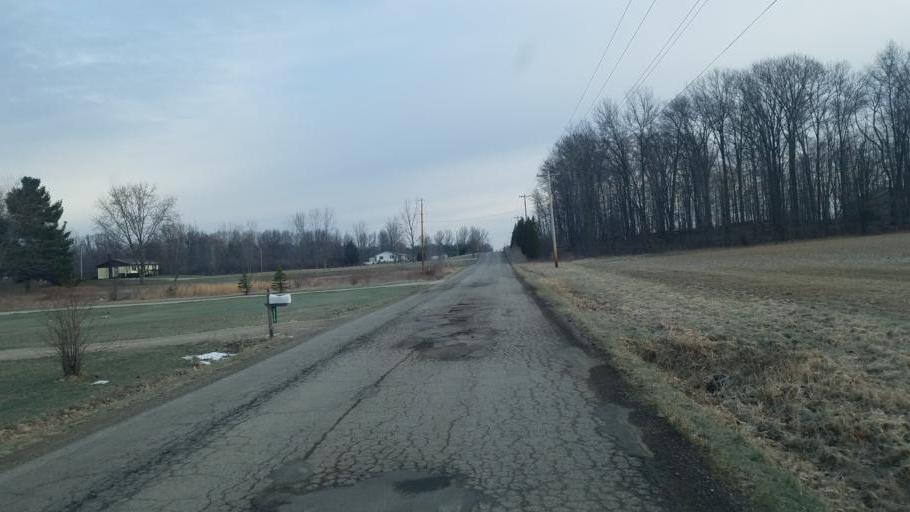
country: US
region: Ohio
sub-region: Morrow County
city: Mount Gilead
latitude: 40.4800
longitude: -82.7816
